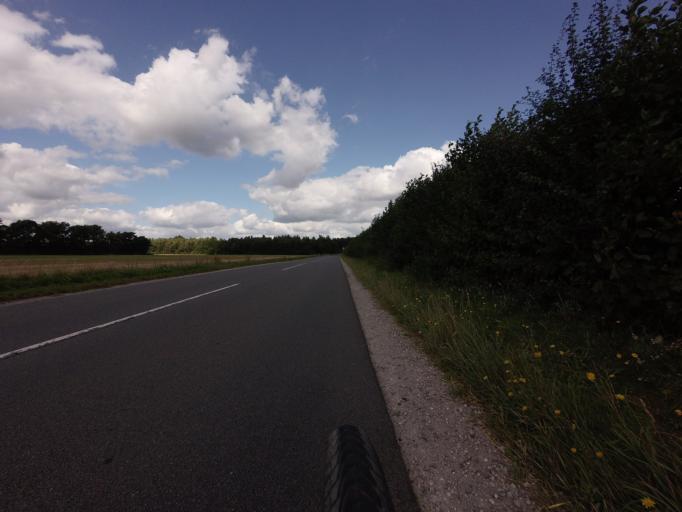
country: DK
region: Central Jutland
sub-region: Ikast-Brande Kommune
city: Brande
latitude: 55.9768
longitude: 9.1449
